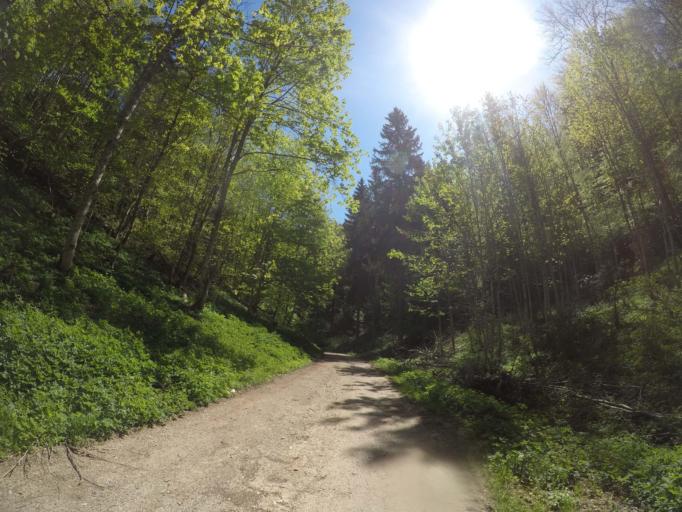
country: DE
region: Baden-Wuerttemberg
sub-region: Tuebingen Region
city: Laichingen
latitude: 48.4274
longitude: 9.6913
